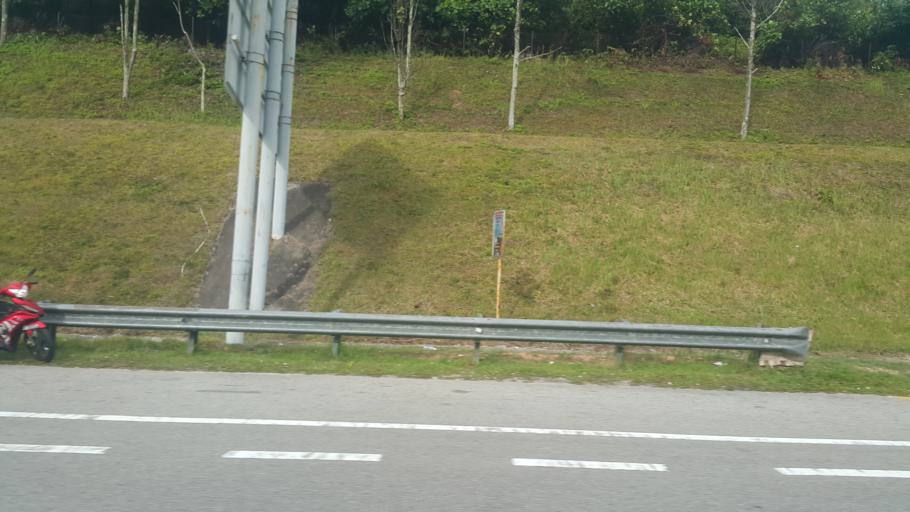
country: MY
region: Johor
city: Pekan Nenas
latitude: 1.3830
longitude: 103.5931
